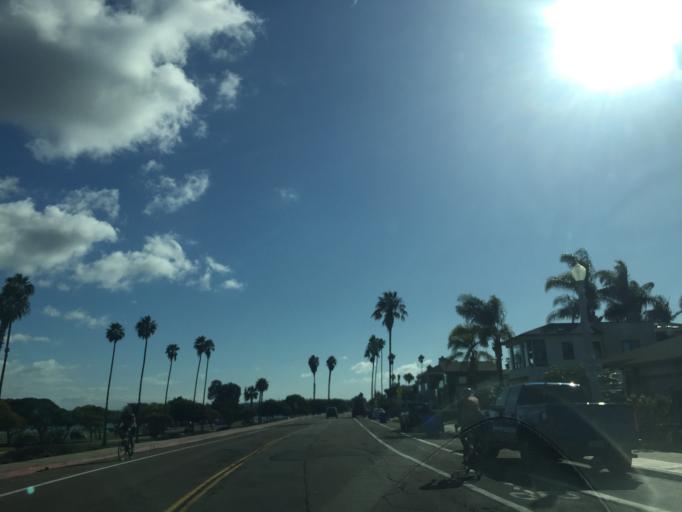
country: US
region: California
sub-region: San Diego County
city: La Jolla
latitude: 32.7862
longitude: -117.2343
